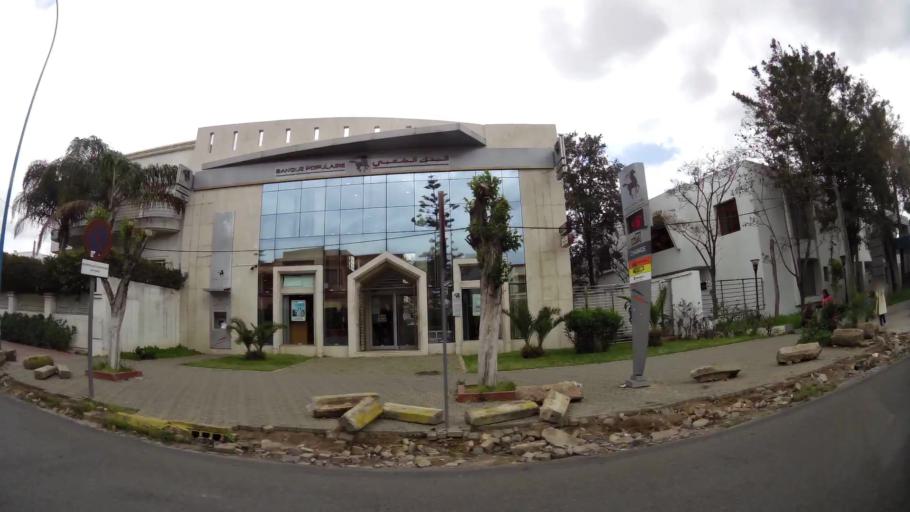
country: MA
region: Grand Casablanca
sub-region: Casablanca
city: Casablanca
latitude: 33.5596
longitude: -7.6119
